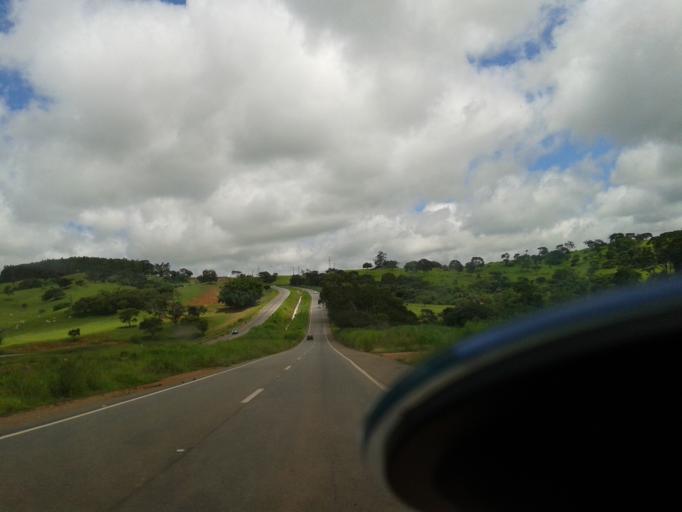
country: BR
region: Goias
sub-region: Inhumas
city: Inhumas
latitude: -16.1674
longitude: -49.6214
